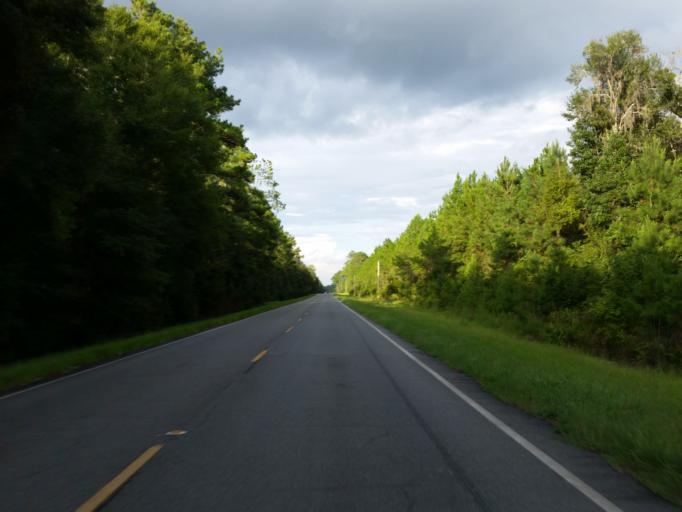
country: US
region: Florida
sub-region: Hamilton County
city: Jasper
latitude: 30.6296
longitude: -82.6011
